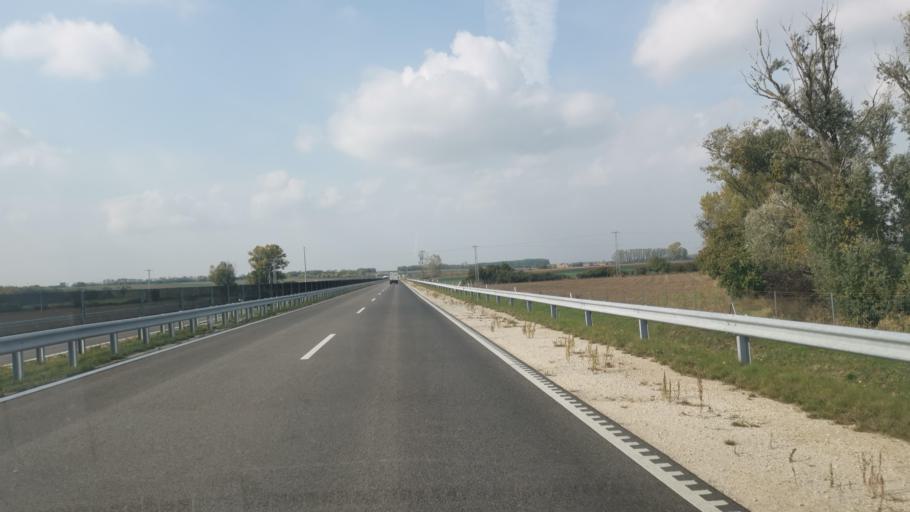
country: HU
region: Gyor-Moson-Sopron
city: Nagycenk
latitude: 47.5759
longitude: 16.7736
